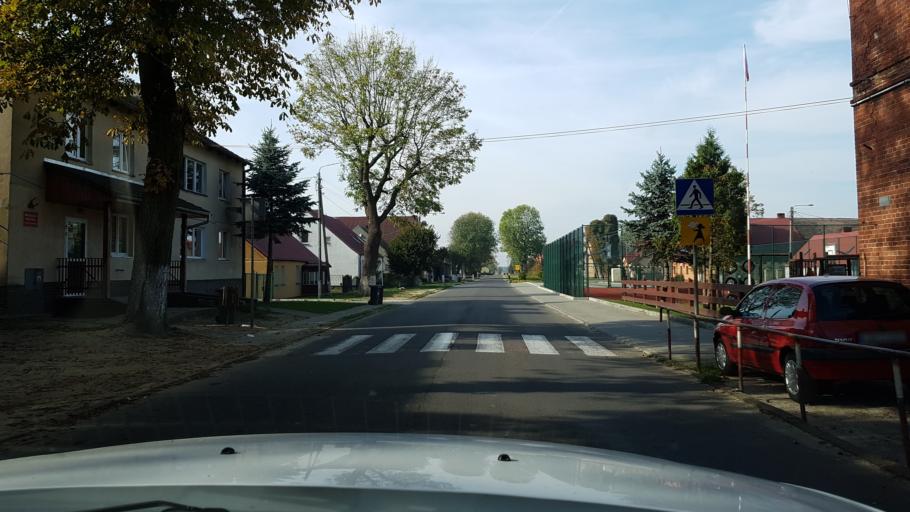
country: PL
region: West Pomeranian Voivodeship
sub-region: Powiat mysliborski
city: Nowogrodek Pomorski
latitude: 52.9596
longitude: 15.1208
